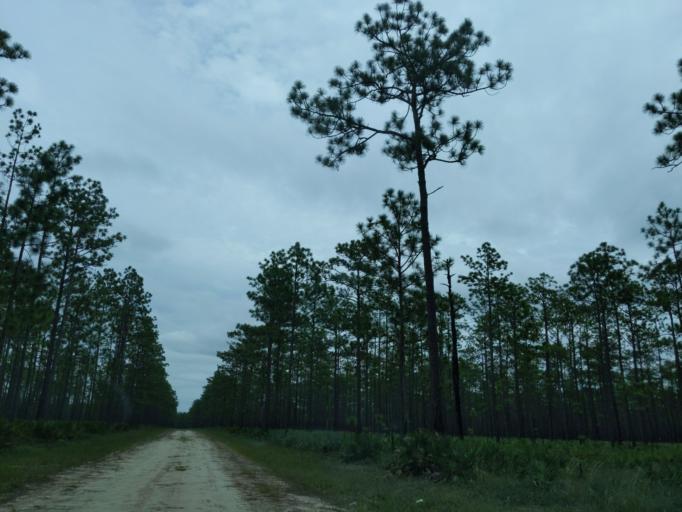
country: US
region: Florida
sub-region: Gadsden County
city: Midway
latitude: 30.3798
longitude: -84.4751
